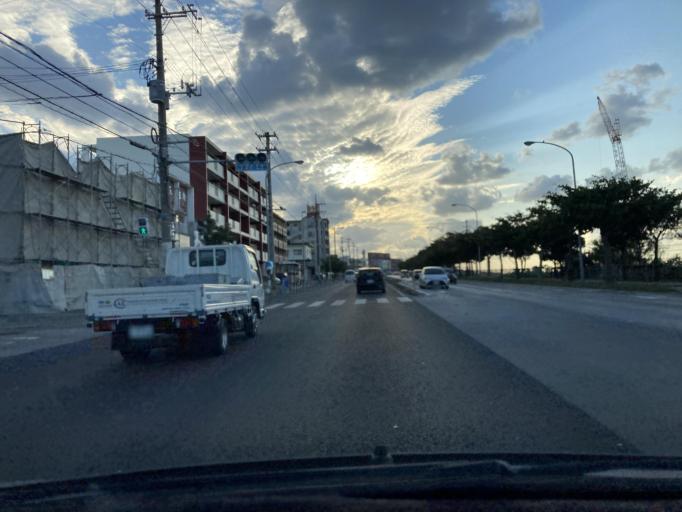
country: JP
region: Okinawa
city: Chatan
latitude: 26.2891
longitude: 127.7695
